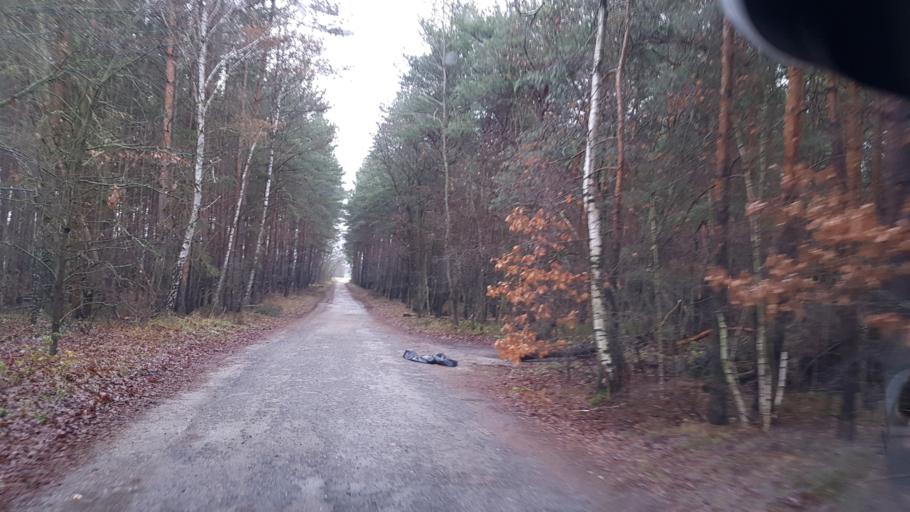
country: DE
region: Brandenburg
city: Sallgast
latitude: 51.6136
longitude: 13.8440
